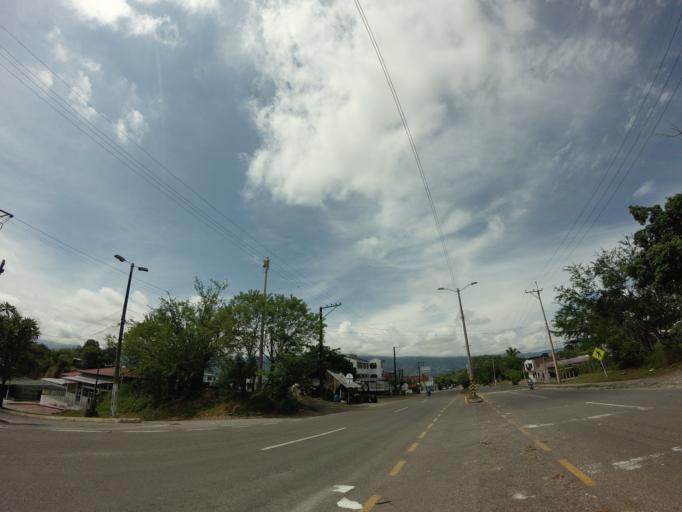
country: CO
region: Caldas
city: La Dorada
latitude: 5.4521
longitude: -74.6738
